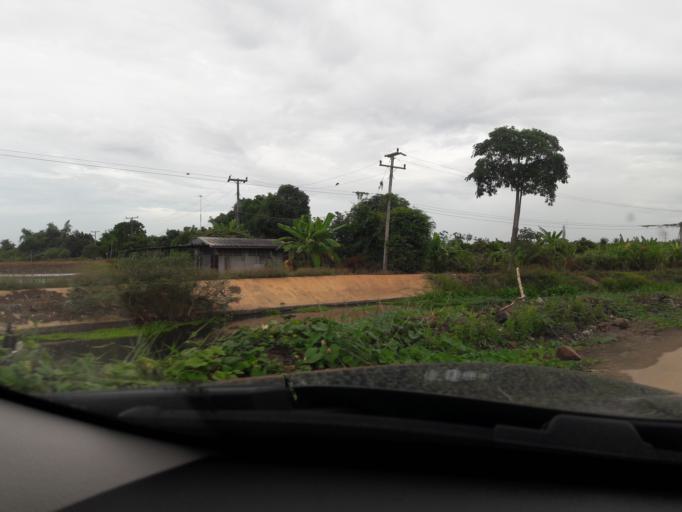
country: TH
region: Ratchaburi
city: Damnoen Saduak
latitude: 13.6076
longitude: 99.9682
